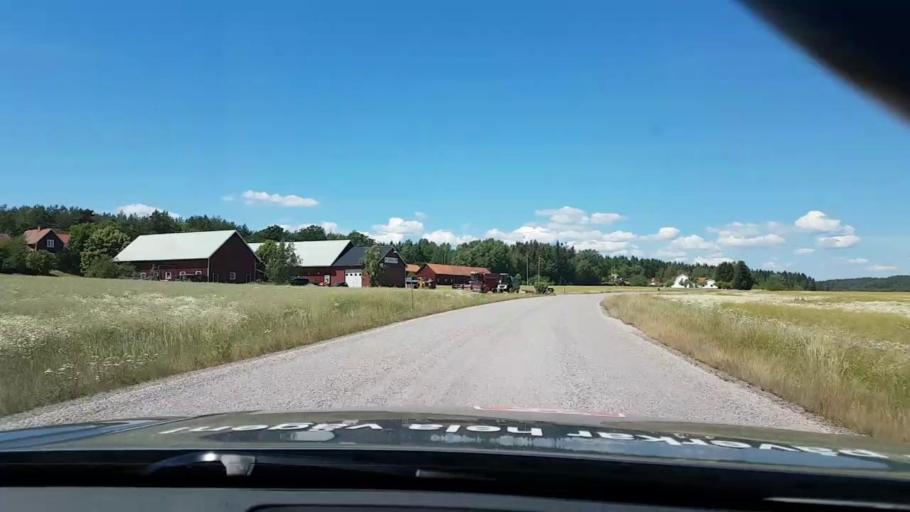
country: SE
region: Kalmar
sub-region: Vasterviks Kommun
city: Forserum
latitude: 57.9402
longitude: 16.4549
